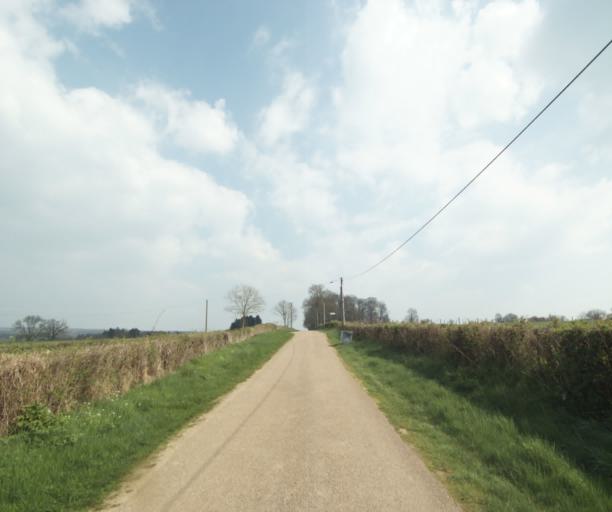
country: FR
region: Bourgogne
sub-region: Departement de Saone-et-Loire
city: Charolles
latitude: 46.4661
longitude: 4.3494
